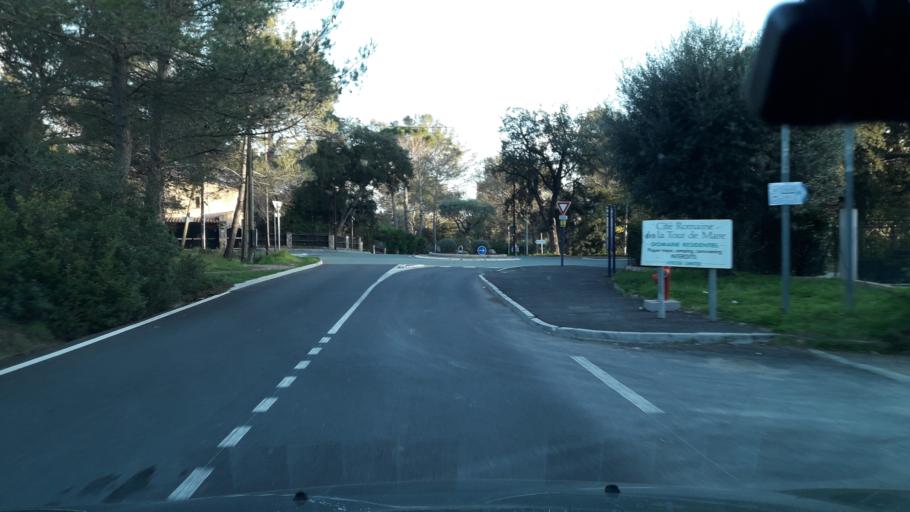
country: FR
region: Provence-Alpes-Cote d'Azur
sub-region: Departement du Var
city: Saint-Raphael
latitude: 43.4629
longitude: 6.7691
